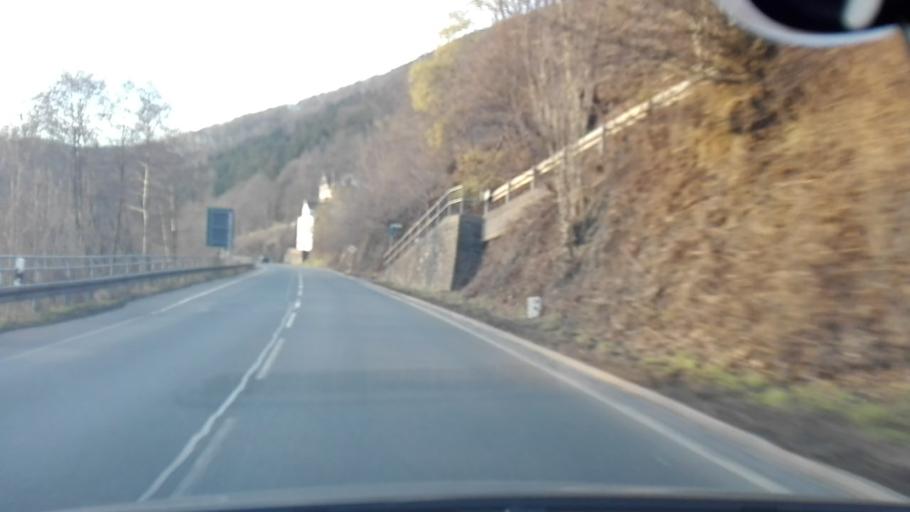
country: DE
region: North Rhine-Westphalia
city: Plettenberg
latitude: 51.2355
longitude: 7.8894
